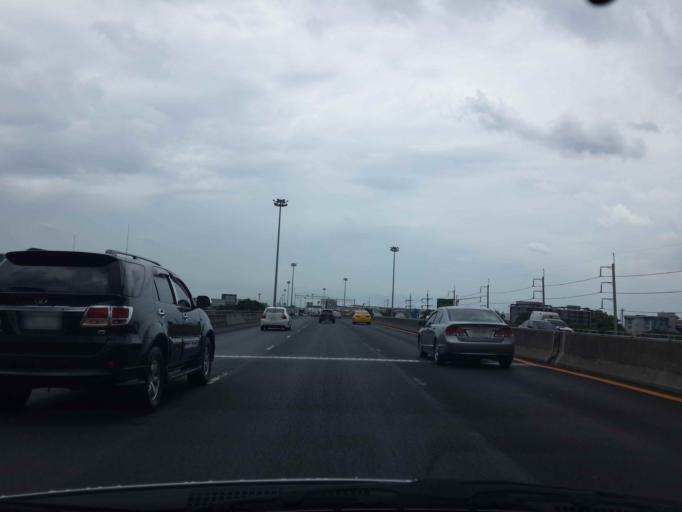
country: TH
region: Bangkok
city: Lat Phrao
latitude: 13.8108
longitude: 100.6200
